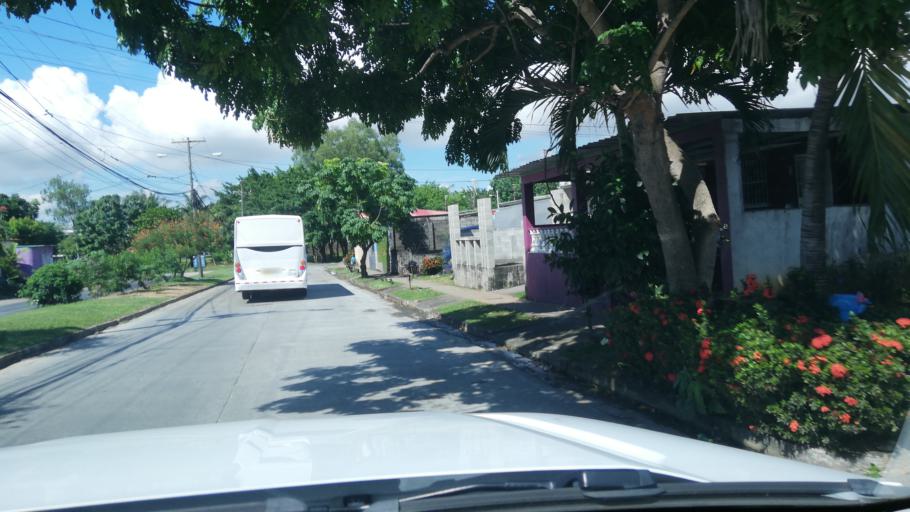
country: PA
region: Panama
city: Tocumen
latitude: 9.0783
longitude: -79.3607
